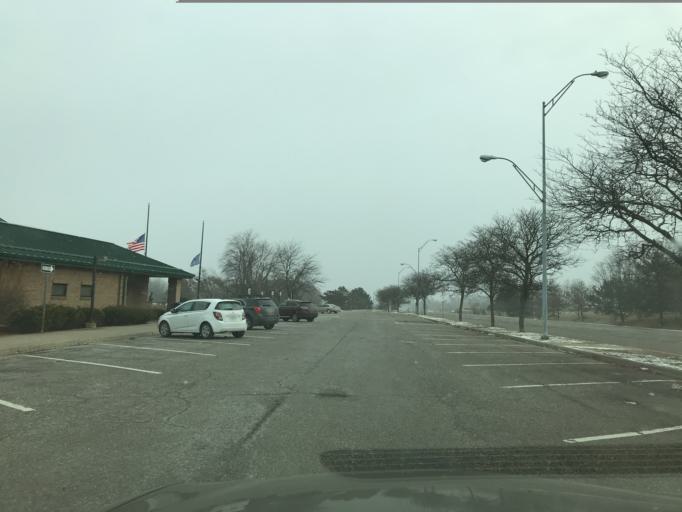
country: US
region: Michigan
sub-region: Clare County
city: Clare
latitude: 43.8507
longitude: -84.7773
